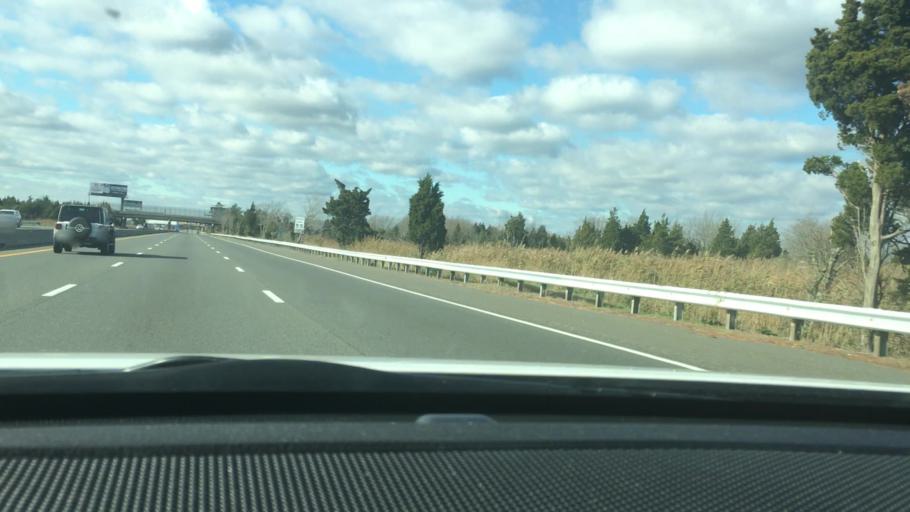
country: US
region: New Jersey
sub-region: Atlantic County
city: Ventnor City
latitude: 39.3741
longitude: -74.4749
